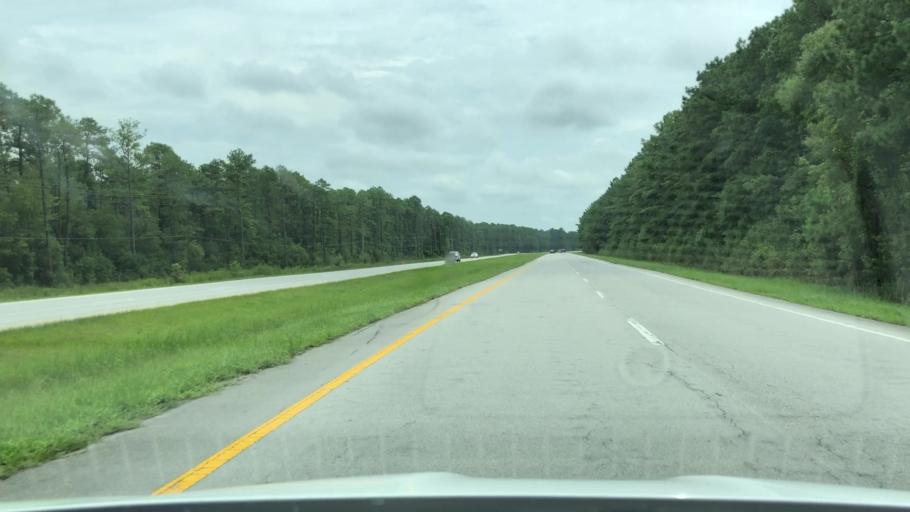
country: US
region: North Carolina
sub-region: Craven County
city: Havelock
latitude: 34.8503
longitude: -76.8879
